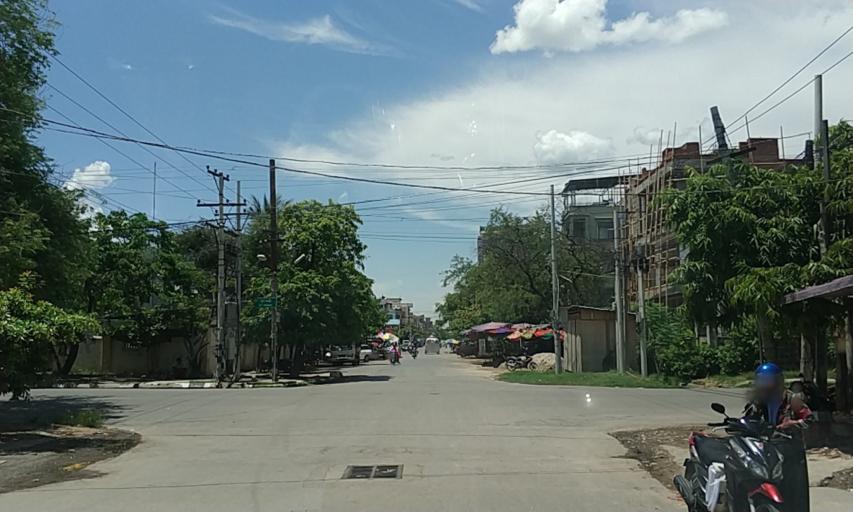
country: MM
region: Mandalay
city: Mandalay
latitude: 21.9746
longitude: 96.0966
